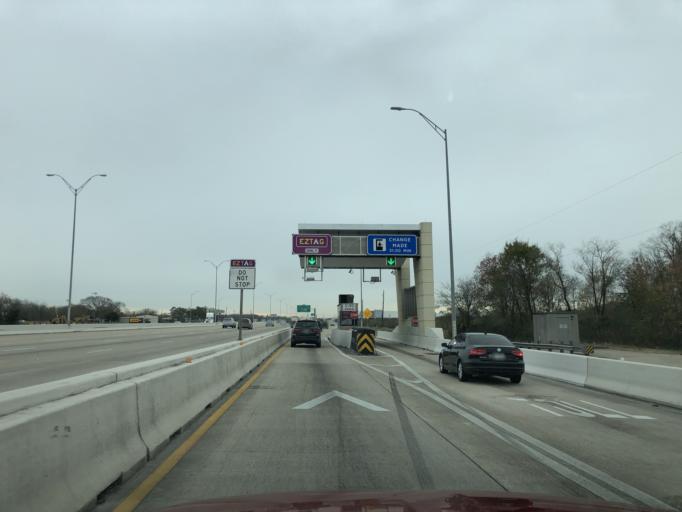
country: US
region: Texas
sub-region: Fort Bend County
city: Missouri City
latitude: 29.6349
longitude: -95.5285
